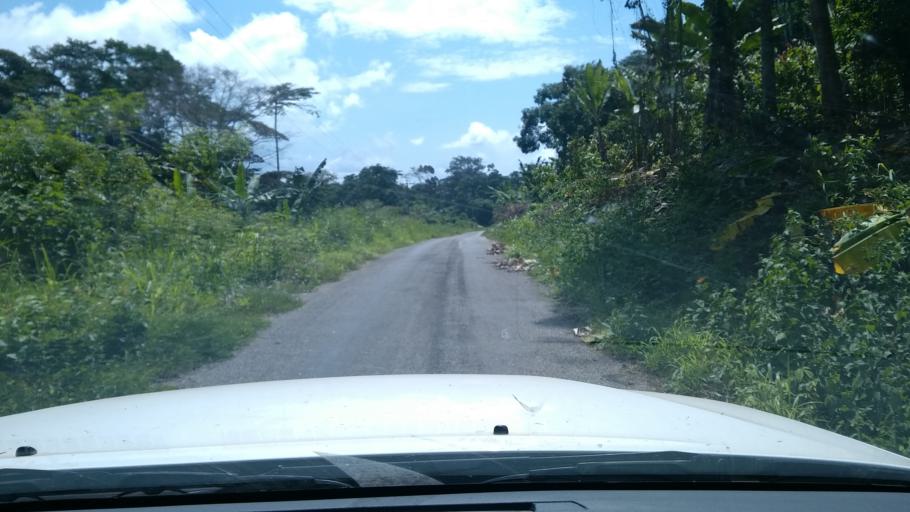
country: CM
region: Centre
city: Evodoula
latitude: 4.1465
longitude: 11.2790
